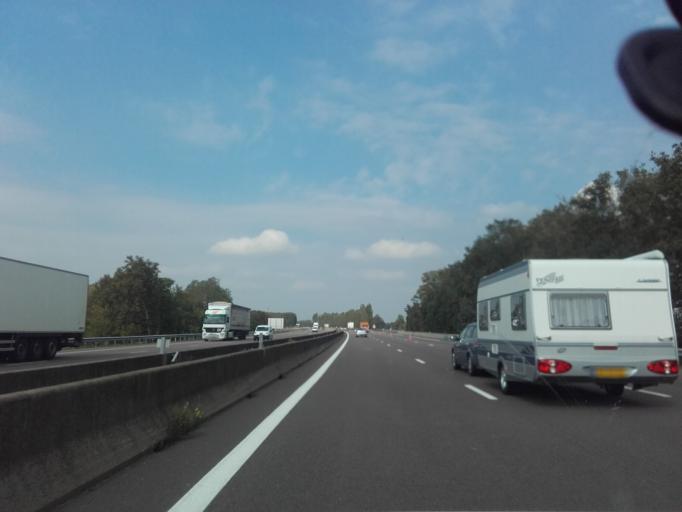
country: FR
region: Bourgogne
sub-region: Departement de Saone-et-Loire
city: Tournus
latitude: 46.5339
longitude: 4.9201
